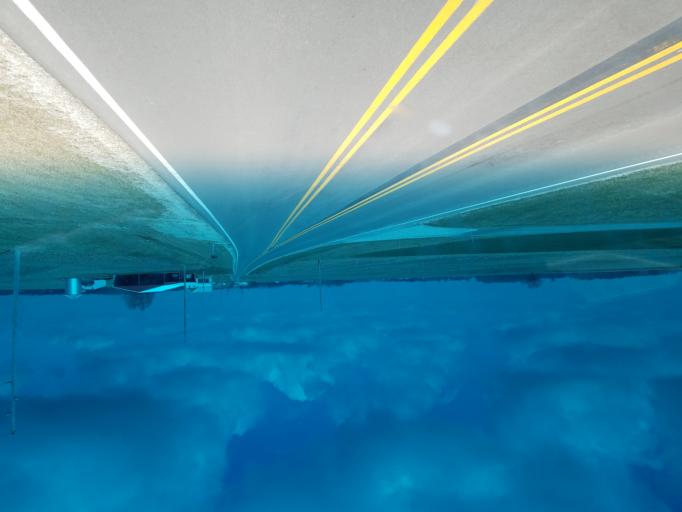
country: US
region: Ohio
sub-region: Crawford County
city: Bucyrus
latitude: 40.7848
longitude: -82.9049
